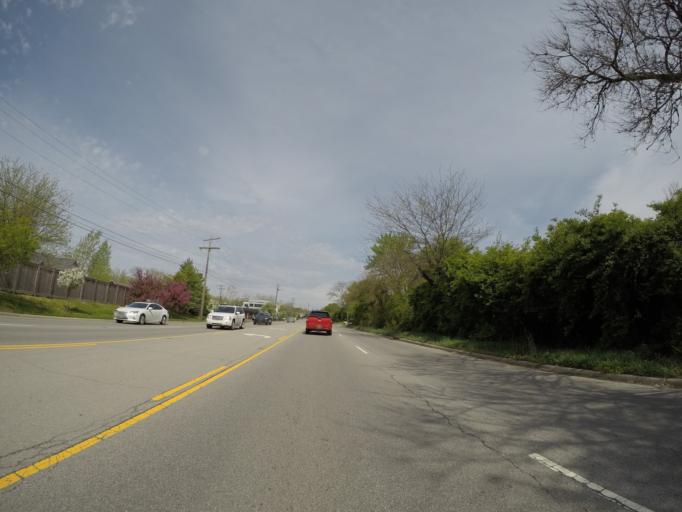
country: US
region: Ohio
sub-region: Franklin County
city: Upper Arlington
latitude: 39.9945
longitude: -83.0707
